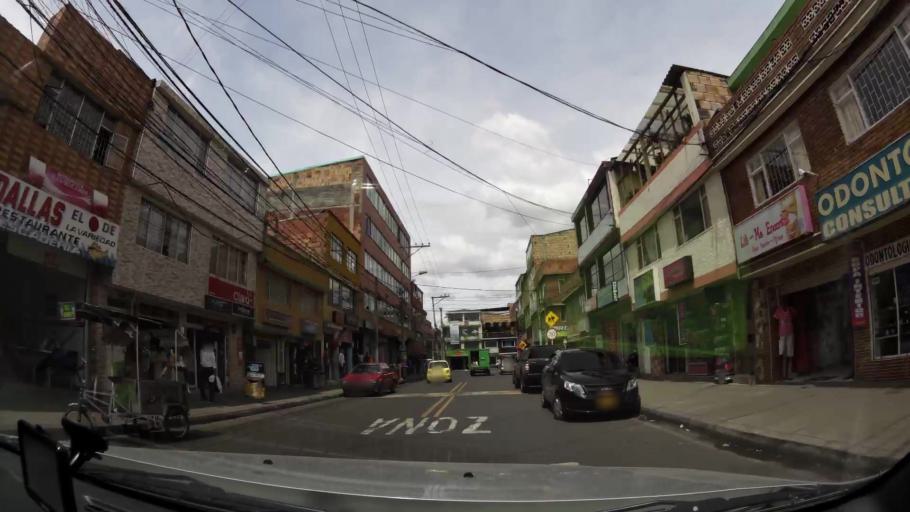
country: CO
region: Cundinamarca
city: Soacha
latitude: 4.6376
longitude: -74.1616
